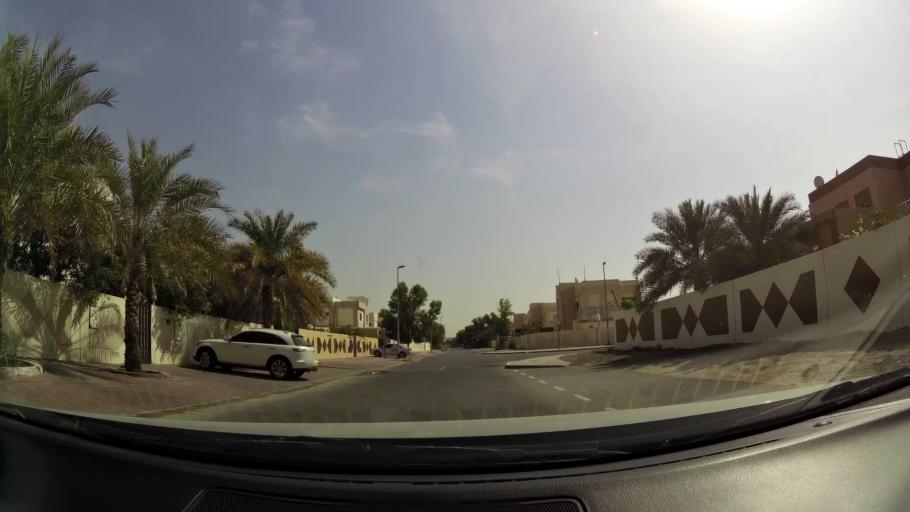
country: AE
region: Ash Shariqah
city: Sharjah
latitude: 25.1970
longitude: 55.4047
